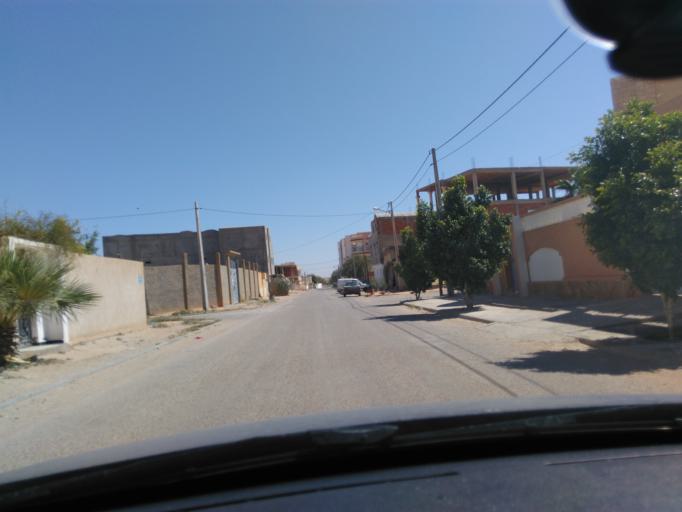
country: TN
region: Tataouine
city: Tataouine
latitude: 32.9483
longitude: 10.4678
